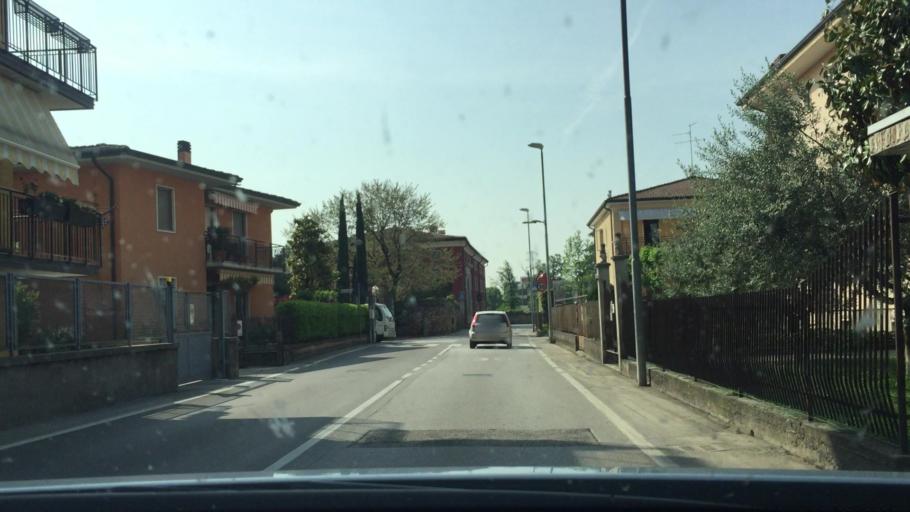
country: IT
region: Veneto
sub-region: Provincia di Verona
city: San Martino Buon Albergo
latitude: 45.4233
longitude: 11.1153
